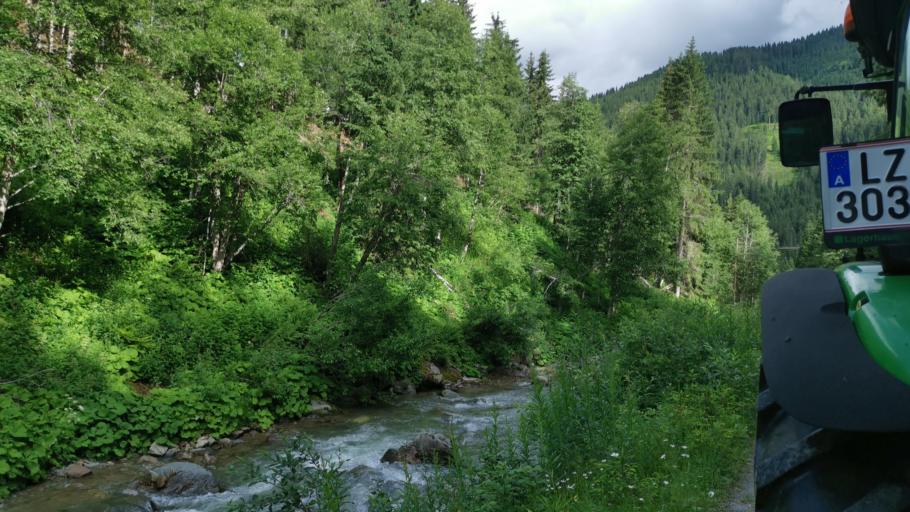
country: AT
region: Tyrol
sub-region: Politischer Bezirk Lienz
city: Obertilliach
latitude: 46.7027
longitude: 12.6053
